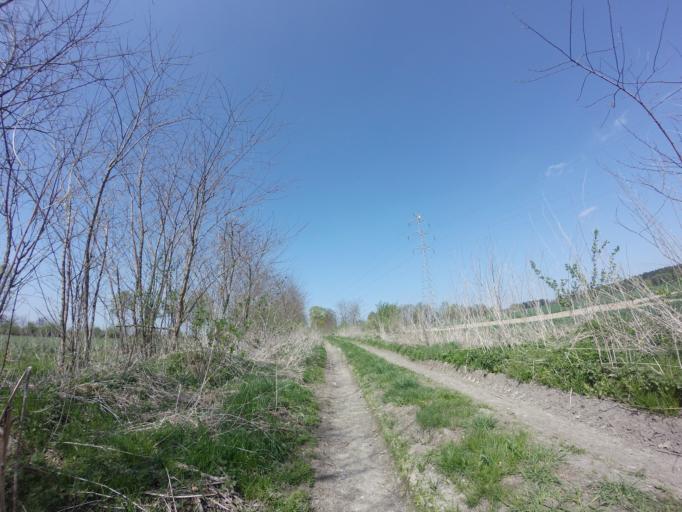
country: PL
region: West Pomeranian Voivodeship
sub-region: Powiat stargardzki
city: Suchan
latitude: 53.2121
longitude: 15.3551
